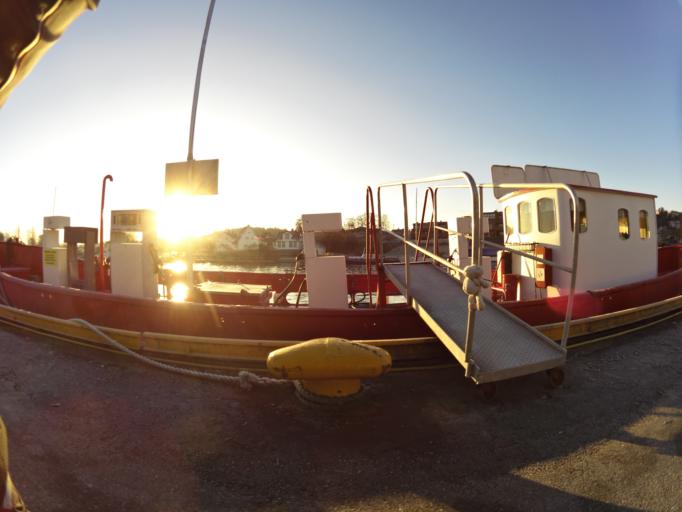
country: NO
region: Ostfold
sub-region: Fredrikstad
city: Fredrikstad
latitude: 59.2056
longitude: 10.9414
